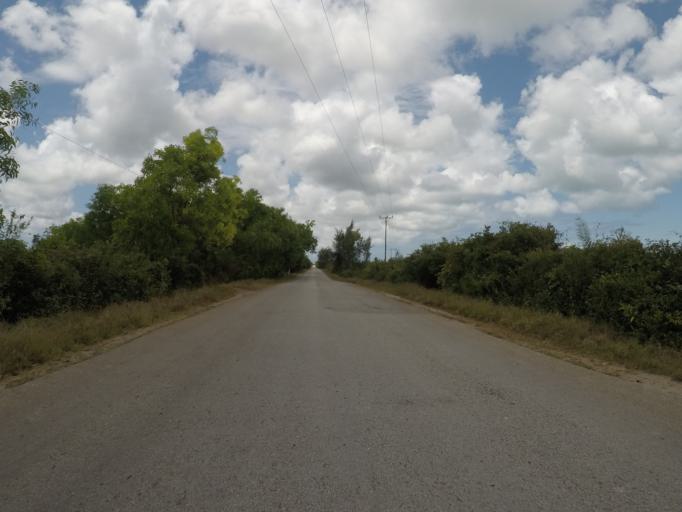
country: TZ
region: Zanzibar Central/South
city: Mahonda
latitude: -6.3172
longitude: 39.4331
